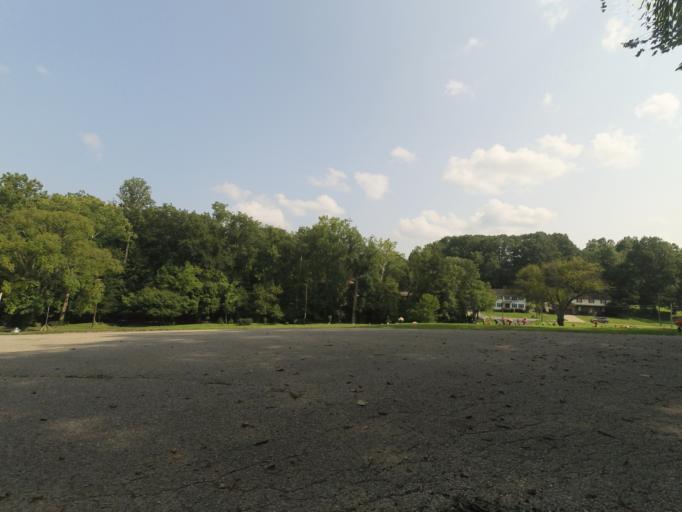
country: US
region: West Virginia
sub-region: Cabell County
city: Huntington
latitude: 38.4041
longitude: -82.3942
